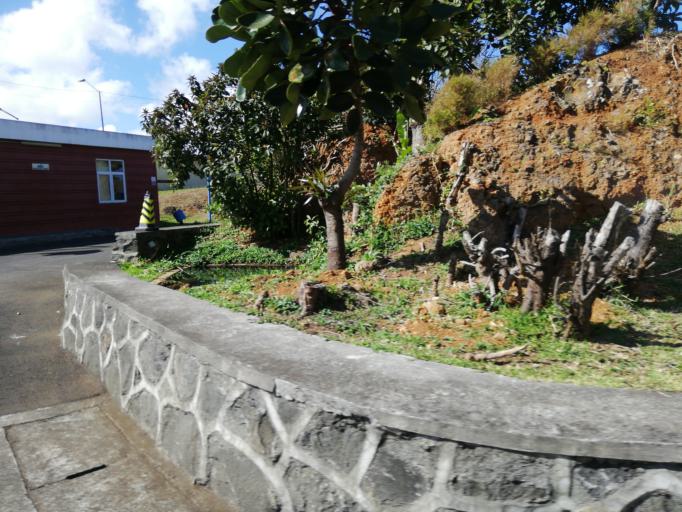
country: MU
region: Moka
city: Moka
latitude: -20.2301
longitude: 57.5023
